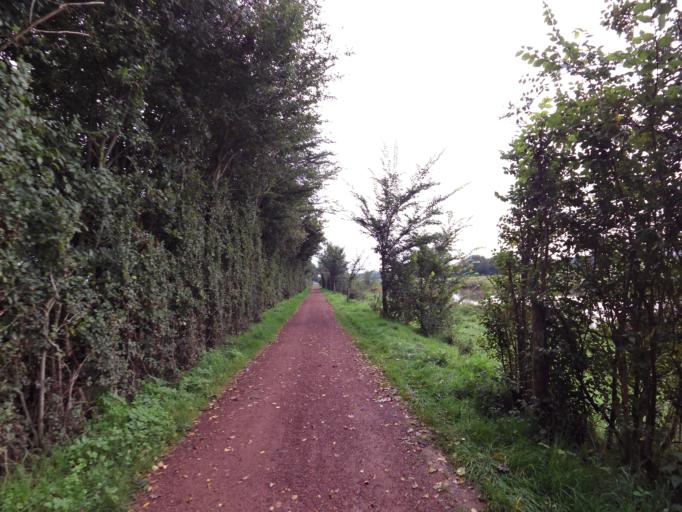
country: DE
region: North Rhine-Westphalia
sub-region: Regierungsbezirk Munster
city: Isselburg
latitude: 51.8499
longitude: 6.4845
